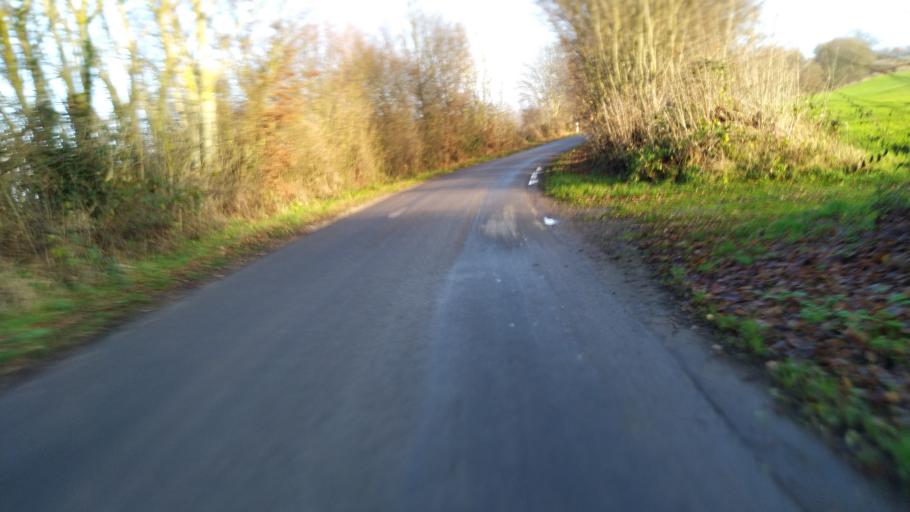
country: DE
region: Schleswig-Holstein
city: Travemuende
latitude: 53.9514
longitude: 10.8305
